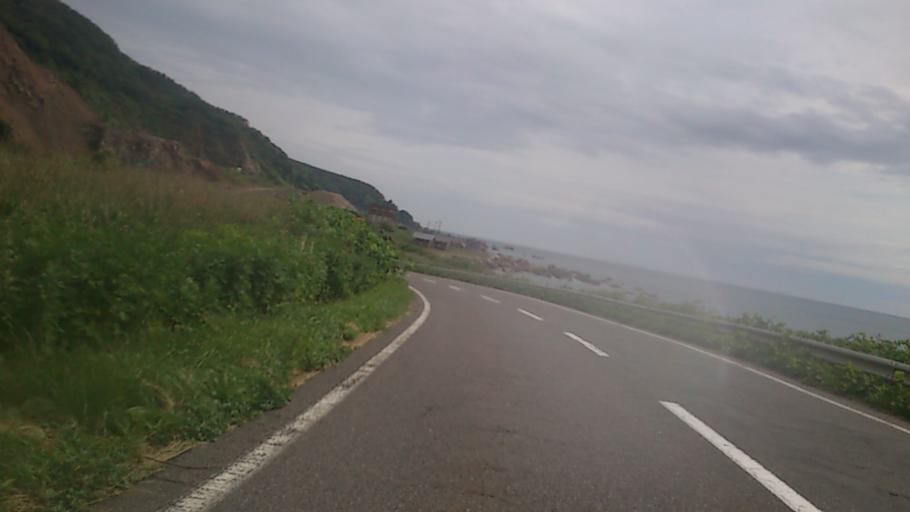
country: JP
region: Akita
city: Noshiromachi
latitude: 40.4625
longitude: 139.9445
